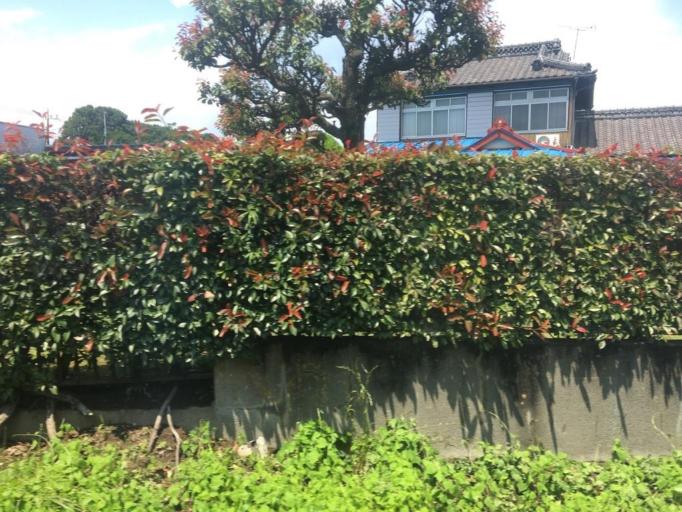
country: JP
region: Gunma
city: Omamacho-omama
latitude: 36.4182
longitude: 139.2587
